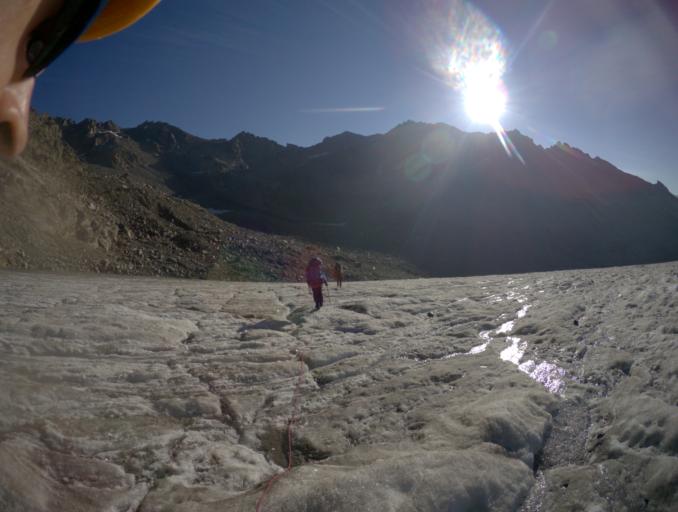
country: RU
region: Kabardino-Balkariya
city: Terskol
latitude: 43.3217
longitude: 42.5247
